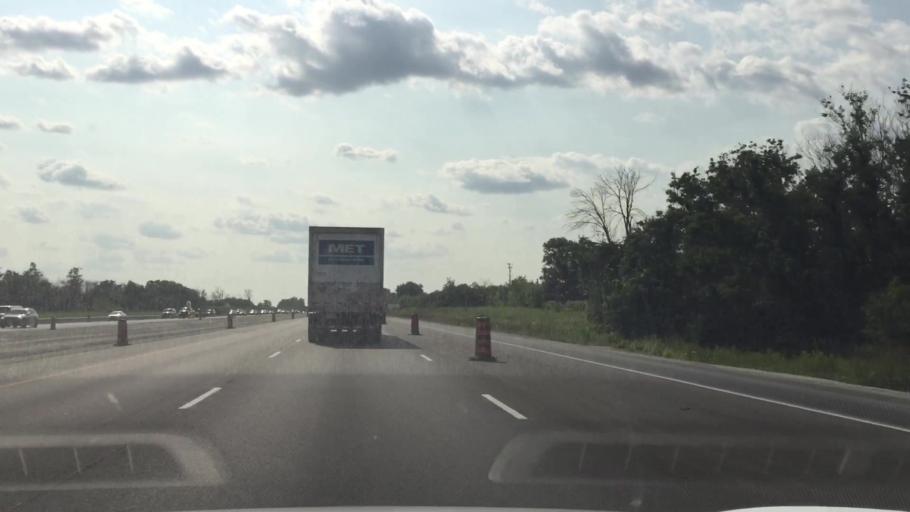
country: CA
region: Ontario
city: Pickering
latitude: 43.9082
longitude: -79.1204
